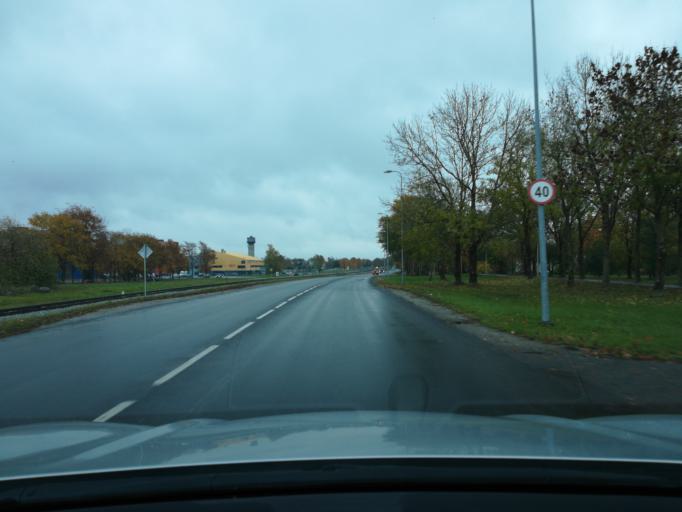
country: EE
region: Ida-Virumaa
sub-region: Johvi vald
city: Johvi
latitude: 59.3285
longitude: 27.4164
